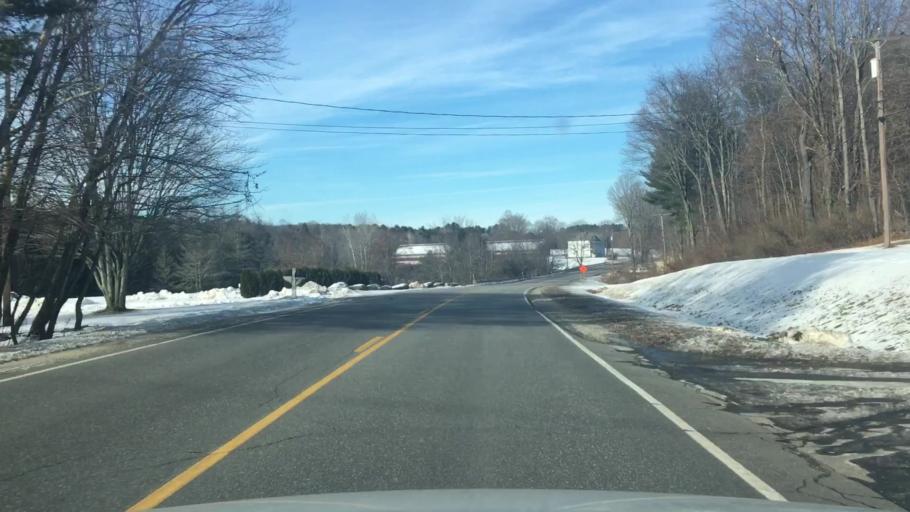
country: US
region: Maine
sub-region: Androscoggin County
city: Lewiston
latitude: 44.0557
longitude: -70.2044
